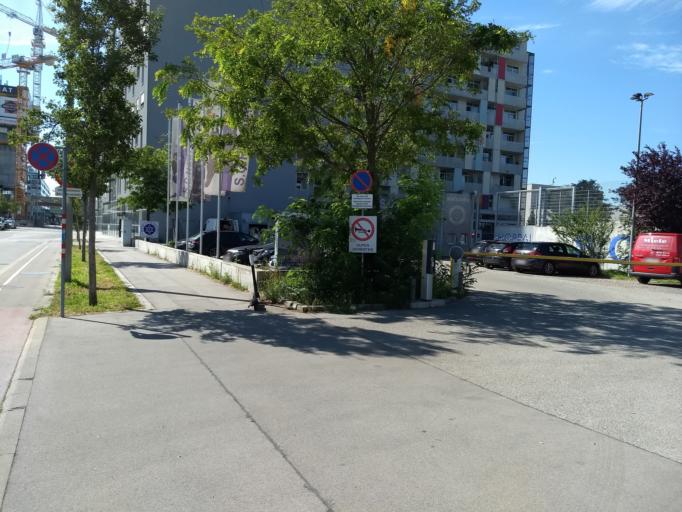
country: AT
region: Vienna
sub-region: Wien Stadt
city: Vienna
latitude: 48.2075
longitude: 16.4284
